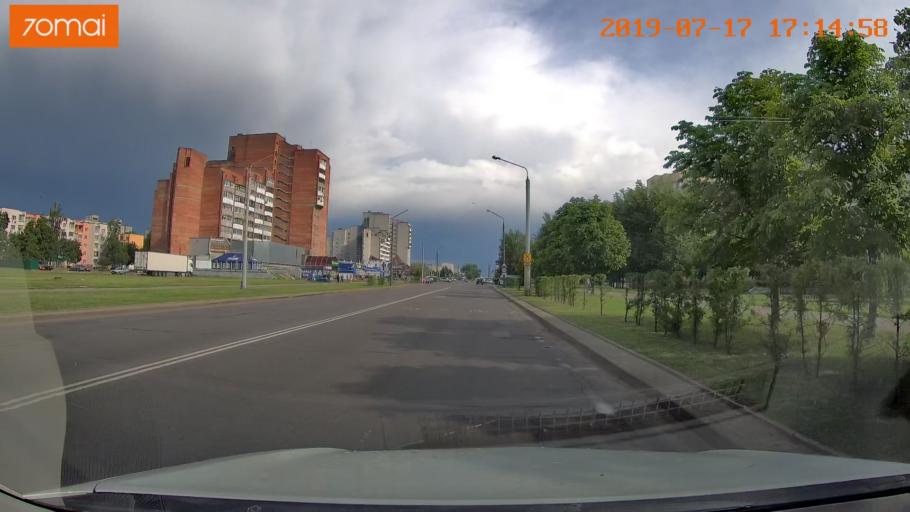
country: BY
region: Mogilev
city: Babruysk
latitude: 53.1725
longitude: 29.1894
